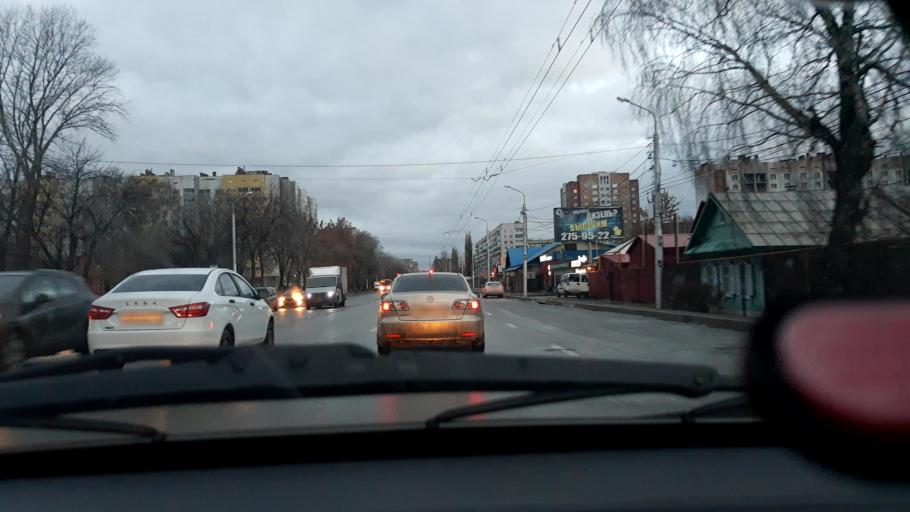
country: RU
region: Bashkortostan
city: Mikhaylovka
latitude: 54.7787
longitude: 55.8898
